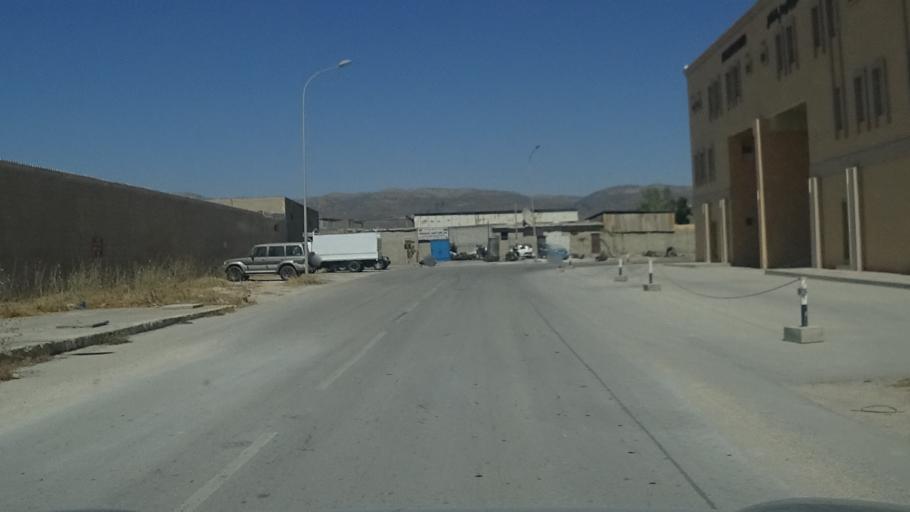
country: OM
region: Zufar
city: Salalah
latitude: 17.0325
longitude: 54.0395
